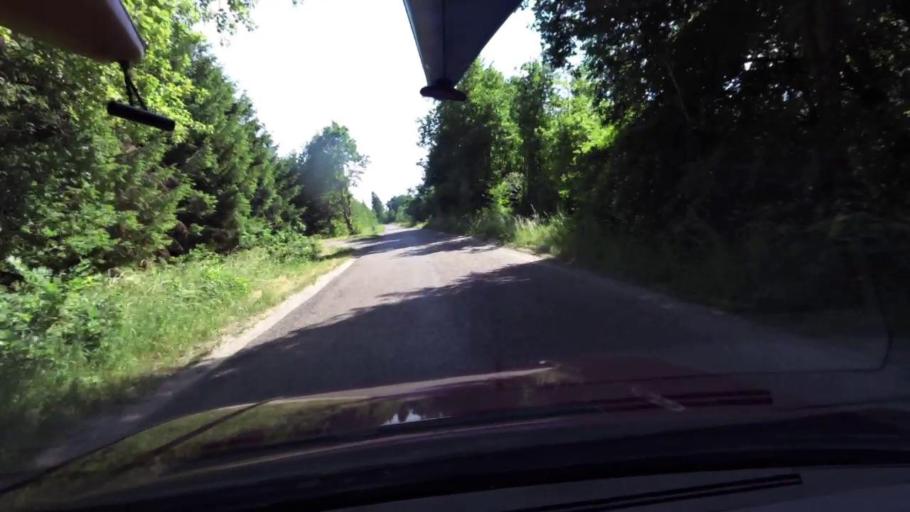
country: PL
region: Pomeranian Voivodeship
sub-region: Powiat slupski
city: Kepice
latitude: 54.1850
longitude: 16.8892
